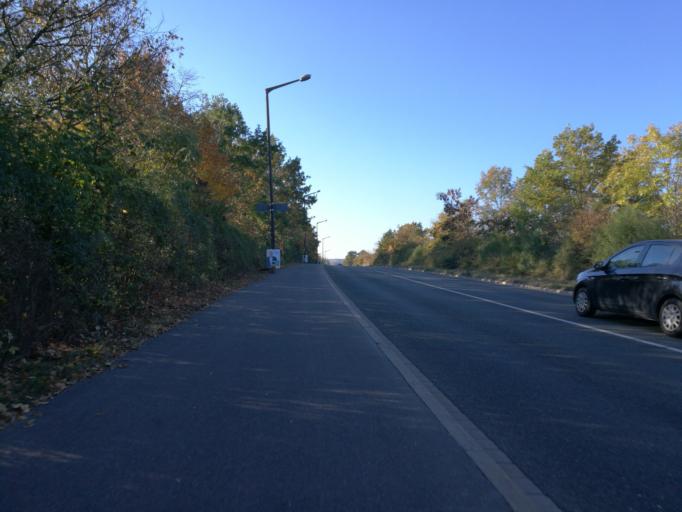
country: DE
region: Bavaria
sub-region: Regierungsbezirk Mittelfranken
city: Veitsbronn
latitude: 49.4953
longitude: 10.9176
